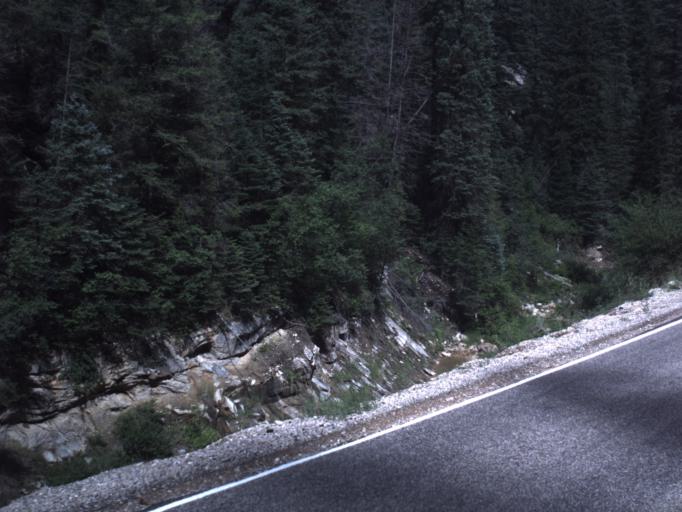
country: US
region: Utah
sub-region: Iron County
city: Cedar City
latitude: 37.6202
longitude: -112.9318
